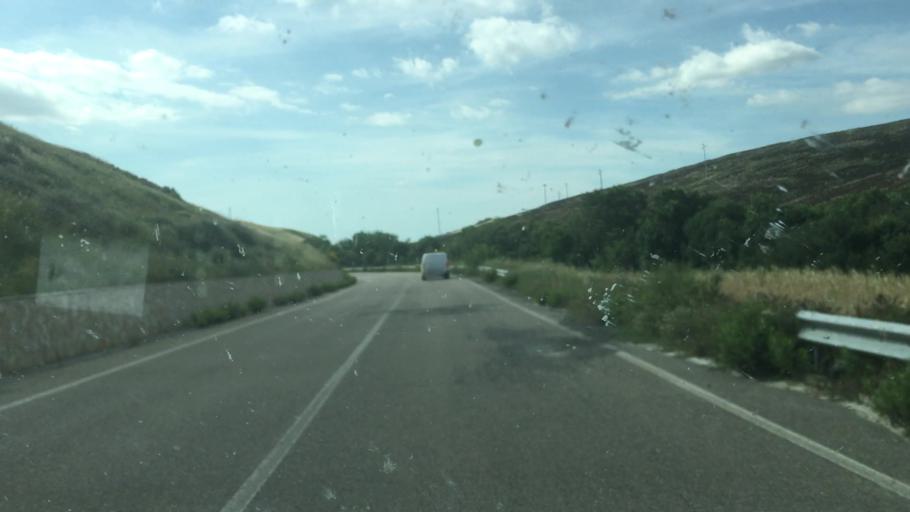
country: IT
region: Basilicate
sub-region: Provincia di Matera
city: Salandra
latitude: 40.5318
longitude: 16.2878
